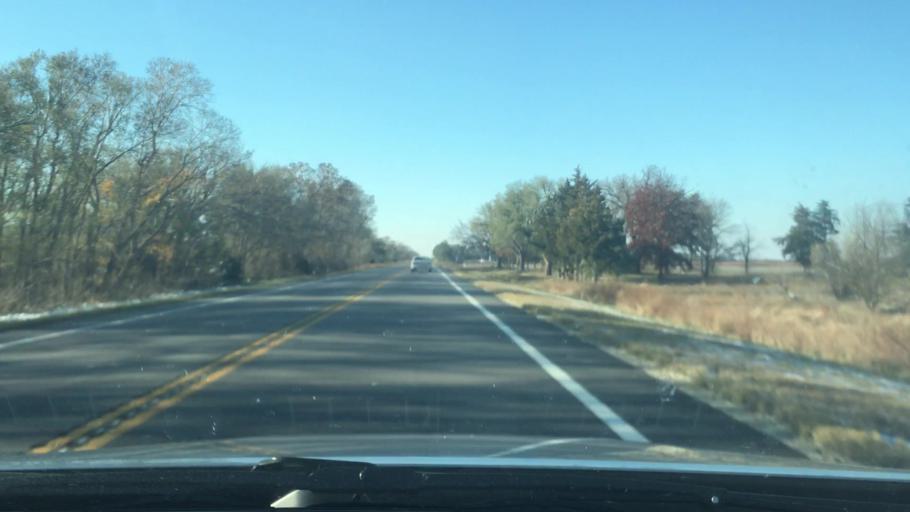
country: US
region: Kansas
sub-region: Reno County
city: Nickerson
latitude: 38.1067
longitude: -98.0241
